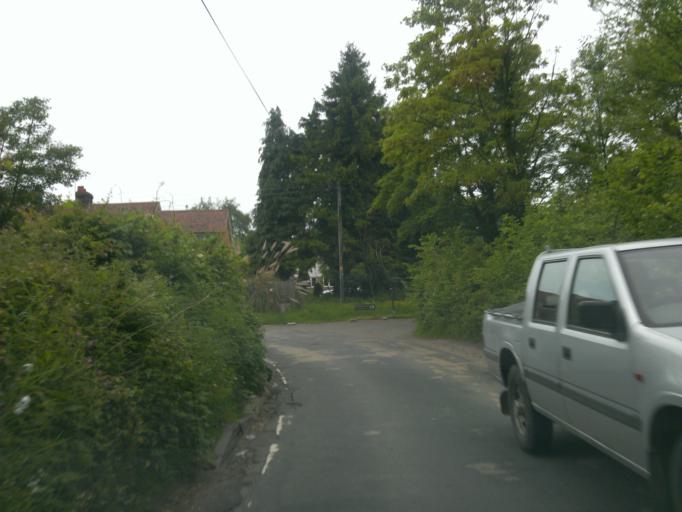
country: GB
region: England
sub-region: Essex
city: West Bergholt
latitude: 51.8956
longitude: 0.8674
